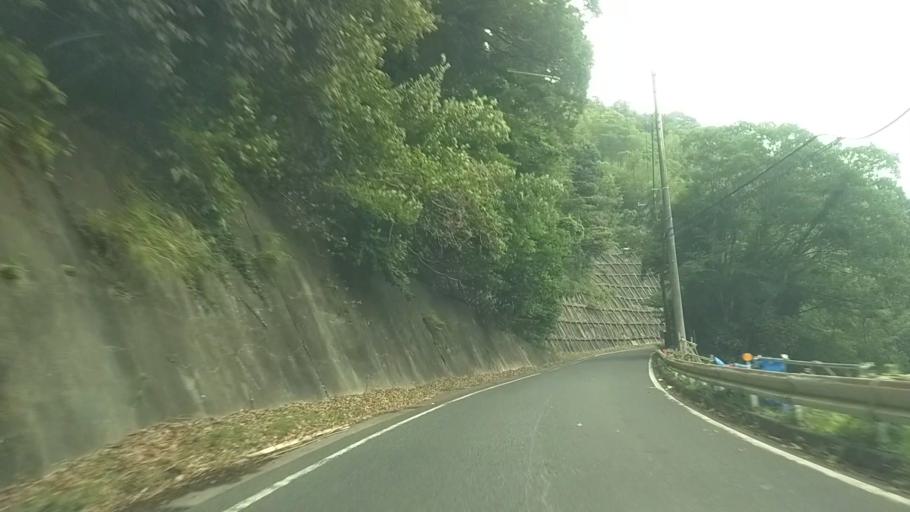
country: JP
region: Chiba
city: Kimitsu
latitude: 35.2496
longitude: 139.9915
